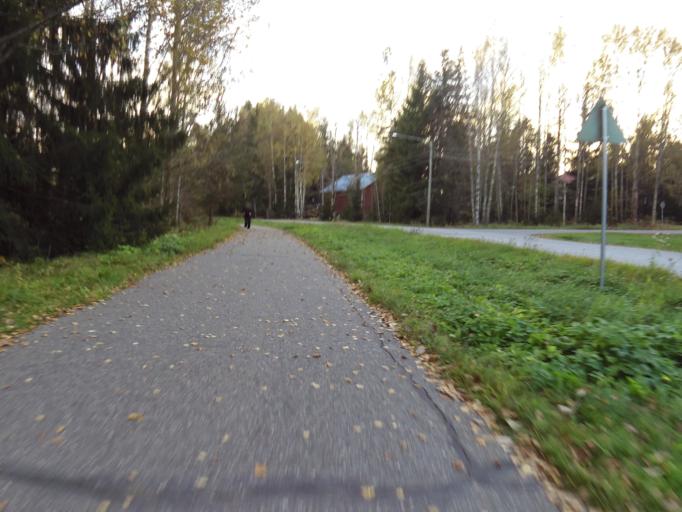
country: FI
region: Uusimaa
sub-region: Helsinki
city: Kauniainen
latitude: 60.3059
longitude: 24.7367
